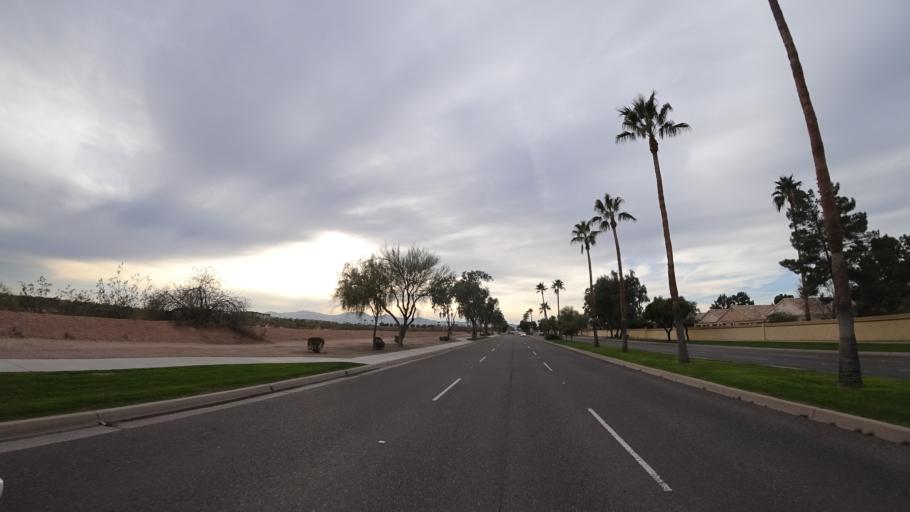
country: US
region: Arizona
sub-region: Maricopa County
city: Sun City West
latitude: 33.6385
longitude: -112.3711
